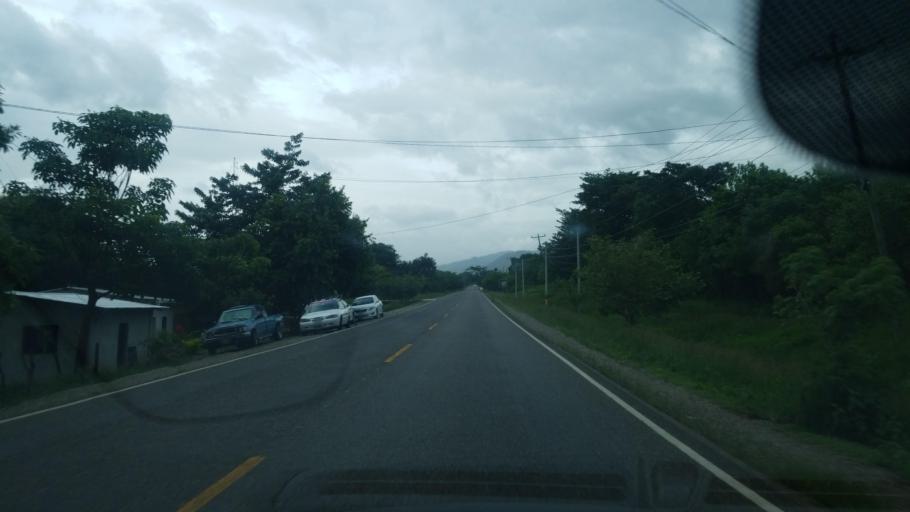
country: HN
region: Ocotepeque
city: Antigua Ocotepeque
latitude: 14.3893
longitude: -89.2049
